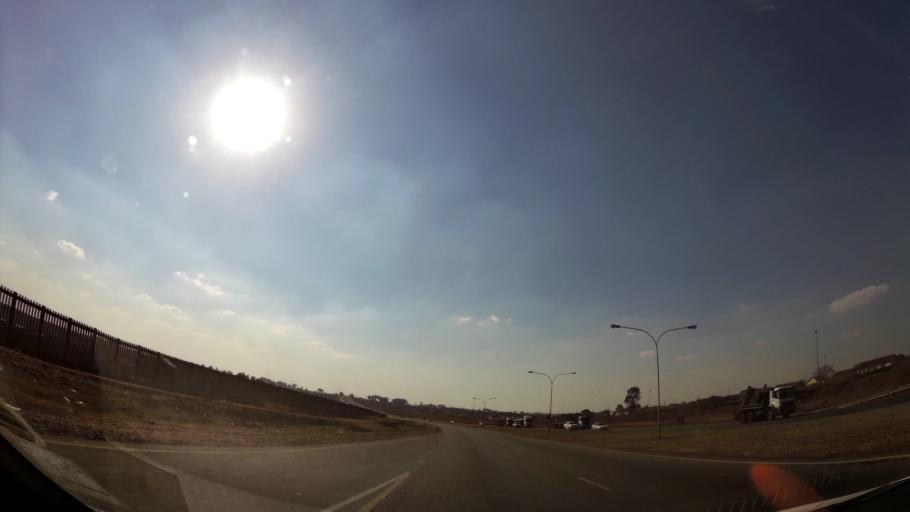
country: ZA
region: Gauteng
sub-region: Ekurhuleni Metropolitan Municipality
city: Benoni
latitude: -26.2326
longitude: 28.3220
